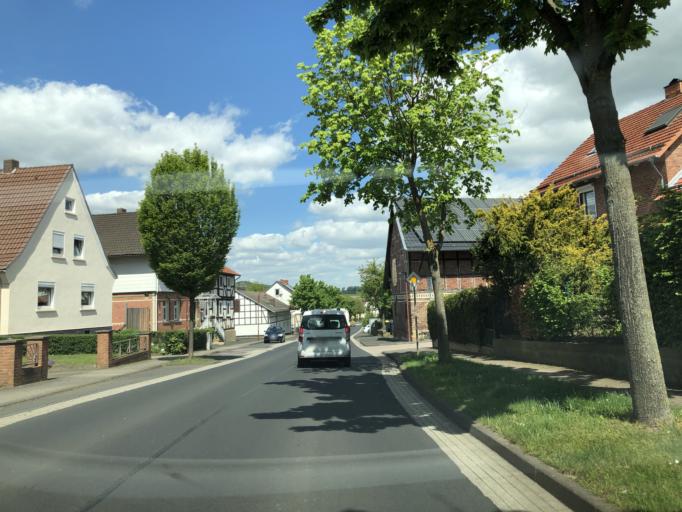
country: DE
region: Hesse
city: Gudensberg
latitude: 51.1485
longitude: 9.3793
